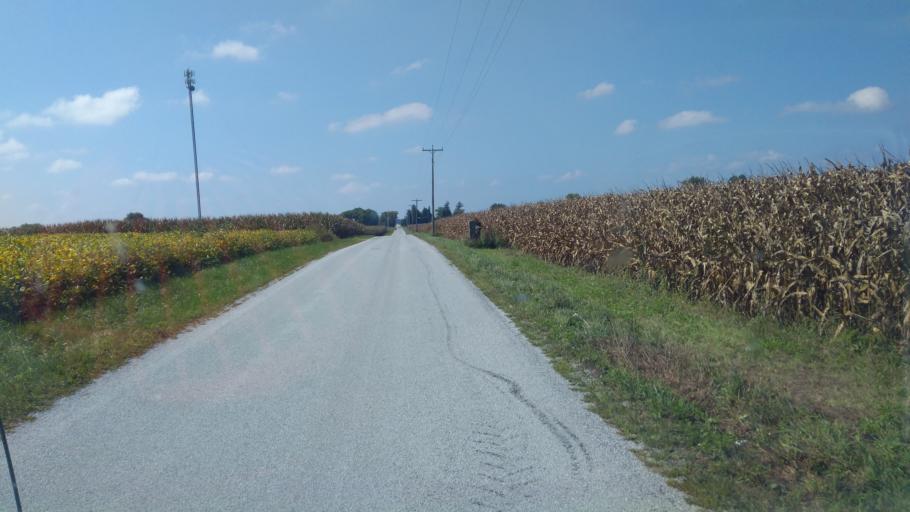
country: US
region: Ohio
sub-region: Hardin County
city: Kenton
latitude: 40.6744
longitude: -83.6041
